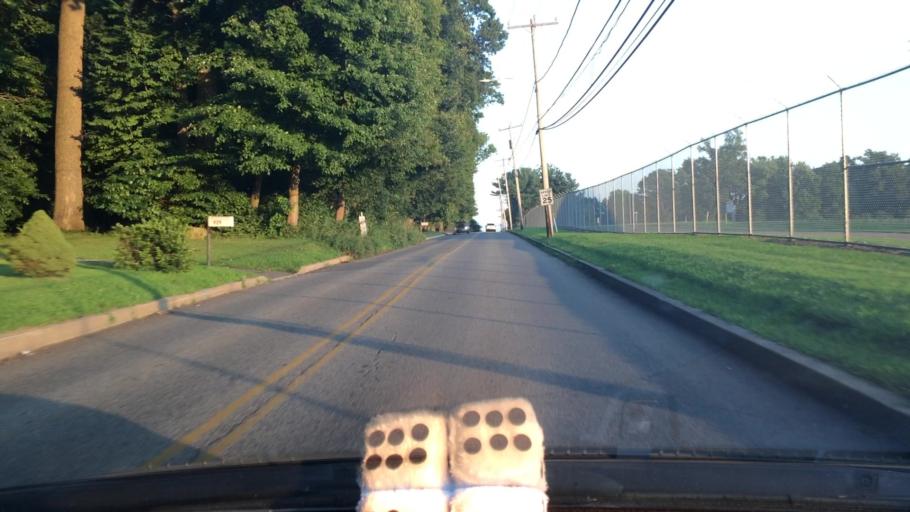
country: US
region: Pennsylvania
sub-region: Delaware County
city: Village Green-Green Ridge
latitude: 39.8610
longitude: -75.4485
